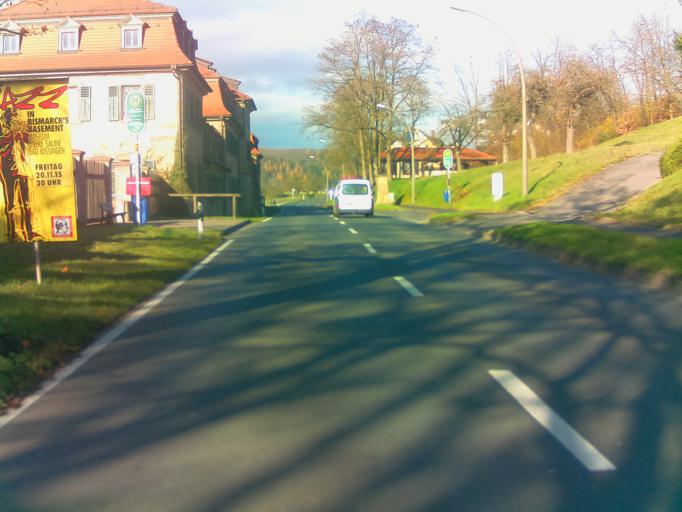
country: DE
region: Bavaria
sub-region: Regierungsbezirk Unterfranken
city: Bad Kissingen
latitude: 50.2209
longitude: 10.0699
